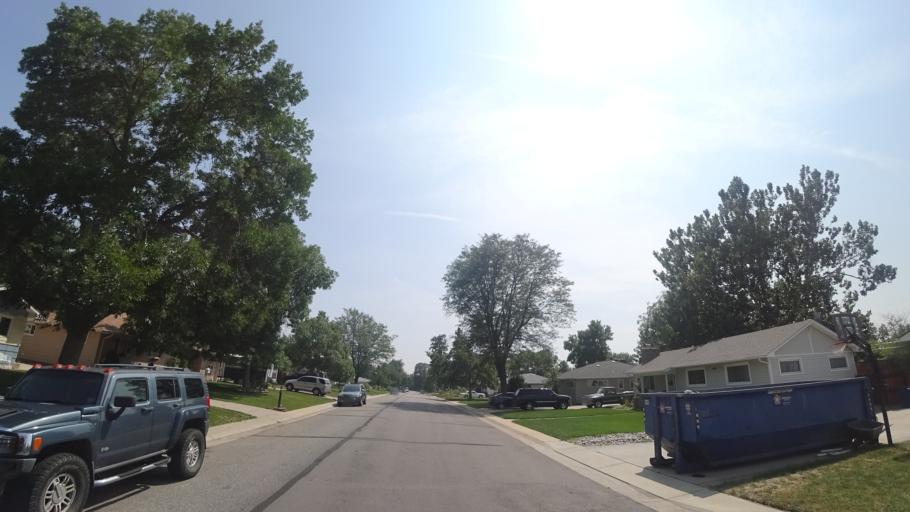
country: US
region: Colorado
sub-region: Arapahoe County
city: Englewood
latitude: 39.6272
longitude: -104.9961
